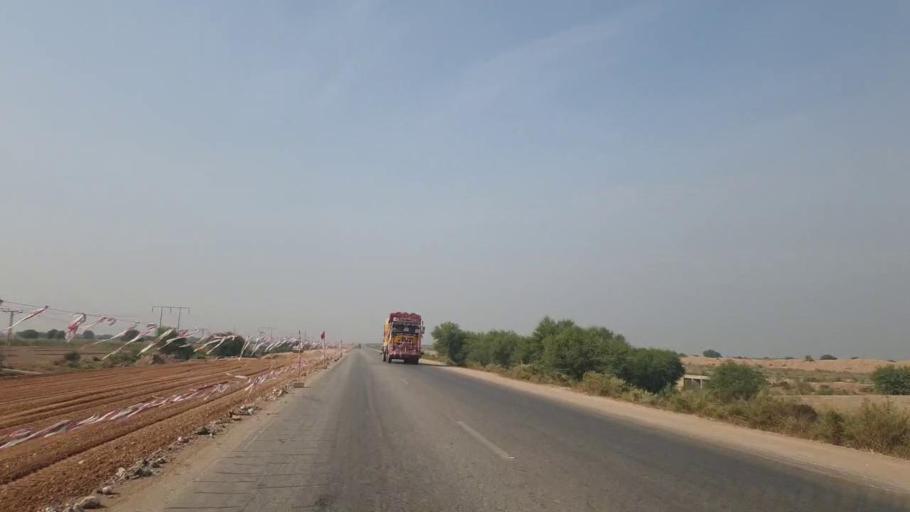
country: PK
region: Sindh
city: Sann
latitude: 26.1460
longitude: 68.0331
